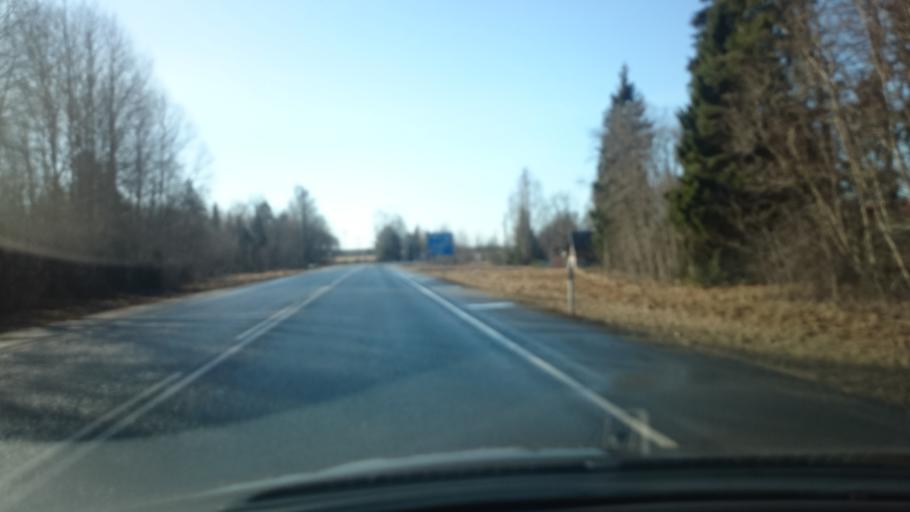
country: EE
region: Raplamaa
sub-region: Rapla vald
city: Rapla
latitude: 59.0441
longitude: 24.8391
